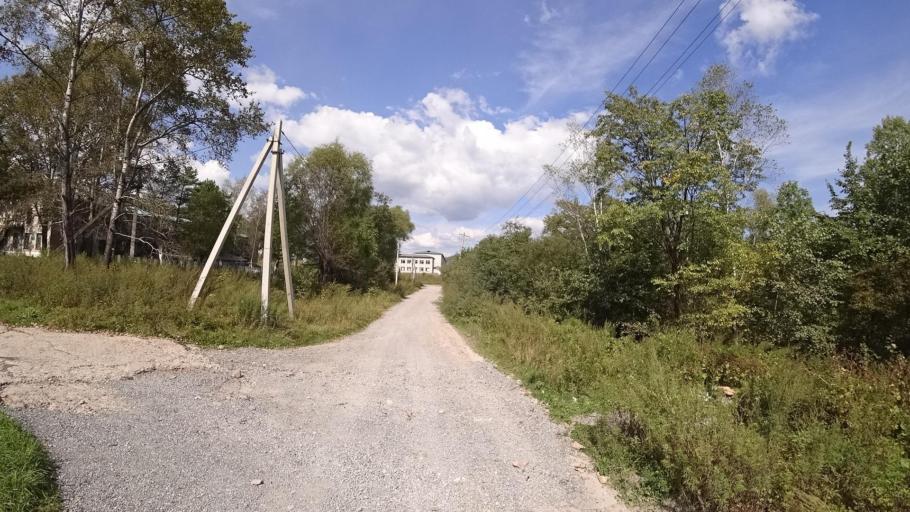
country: RU
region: Jewish Autonomous Oblast
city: Londoko
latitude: 49.0249
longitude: 131.9261
